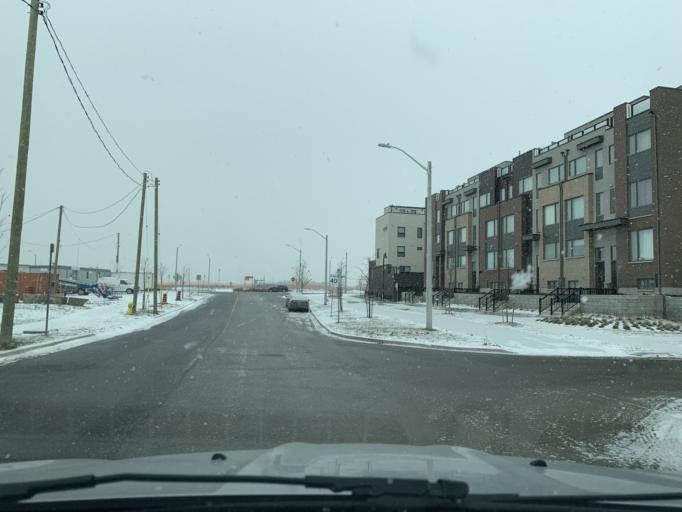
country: CA
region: Ontario
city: Concord
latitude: 43.7353
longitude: -79.4788
